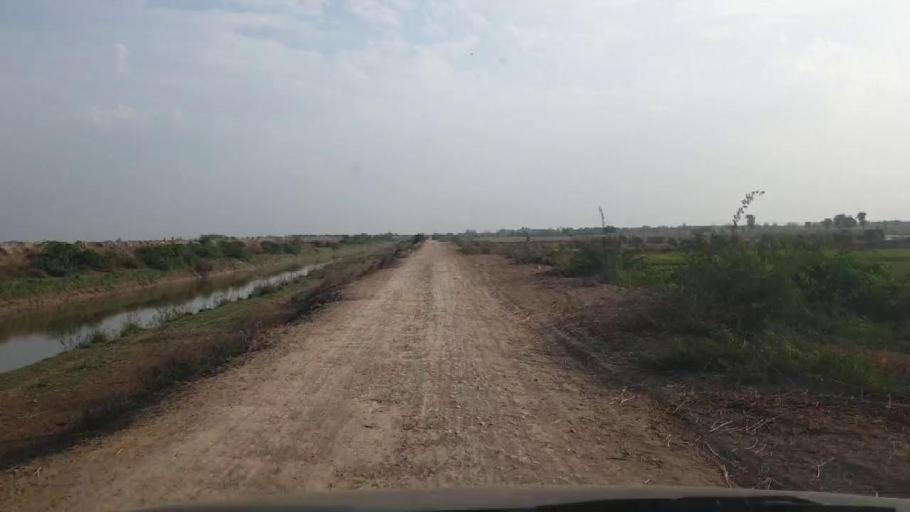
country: PK
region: Sindh
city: Badin
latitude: 24.5591
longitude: 68.6689
